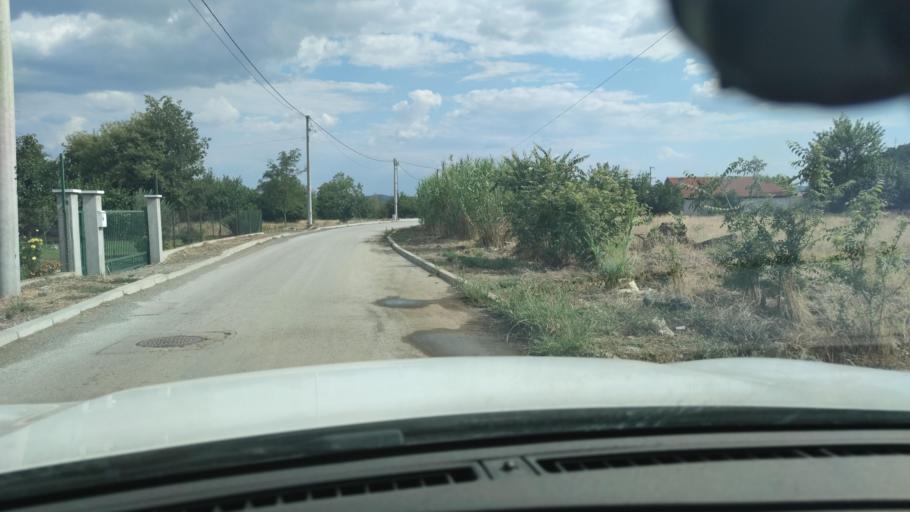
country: MK
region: Gevgelija
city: Gevgelija
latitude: 41.1640
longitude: 22.5055
